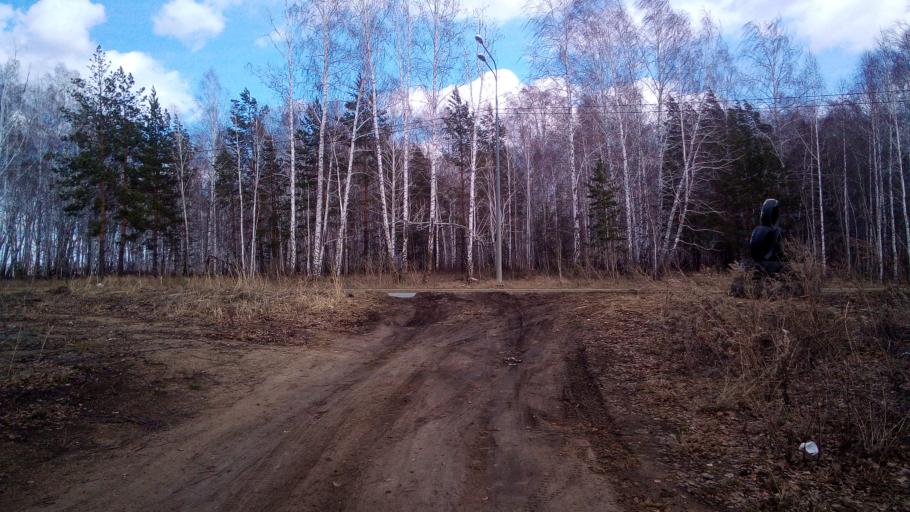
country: RU
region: Chelyabinsk
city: Sargazy
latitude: 55.1239
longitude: 61.2516
